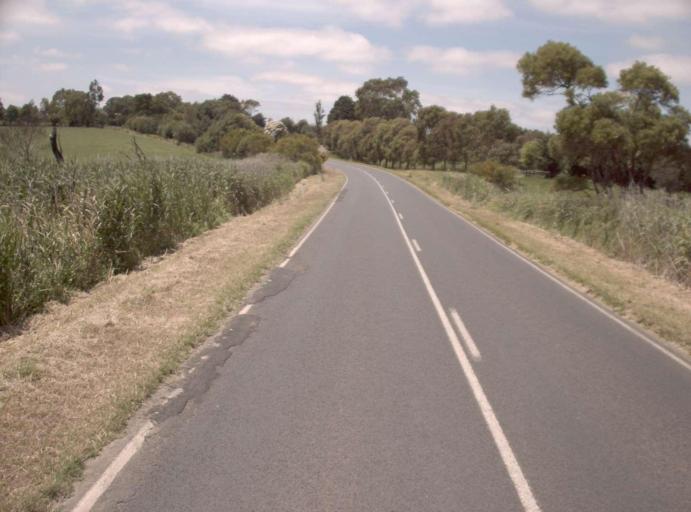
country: AU
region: Victoria
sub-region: Baw Baw
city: Warragul
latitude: -38.4815
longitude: 145.9760
